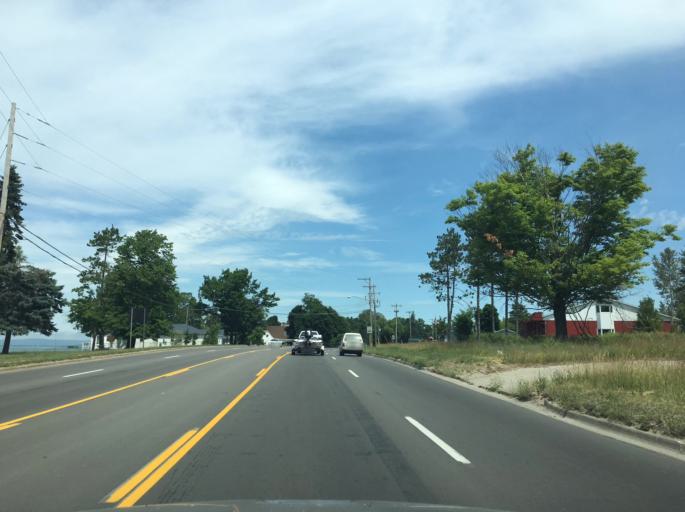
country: US
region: Michigan
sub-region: Grand Traverse County
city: Traverse City
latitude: 44.7685
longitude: -85.5037
